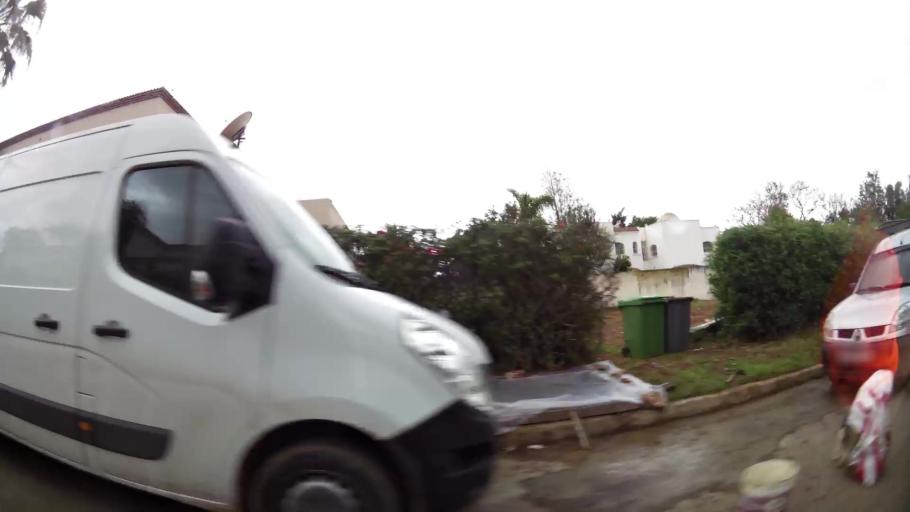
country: MA
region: Grand Casablanca
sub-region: Casablanca
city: Casablanca
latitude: 33.5286
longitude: -7.6329
